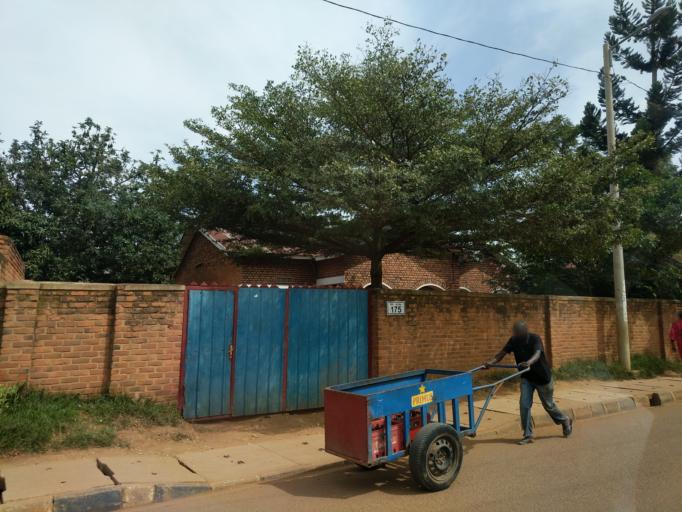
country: RW
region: Kigali
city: Kigali
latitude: -1.9755
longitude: 30.1351
